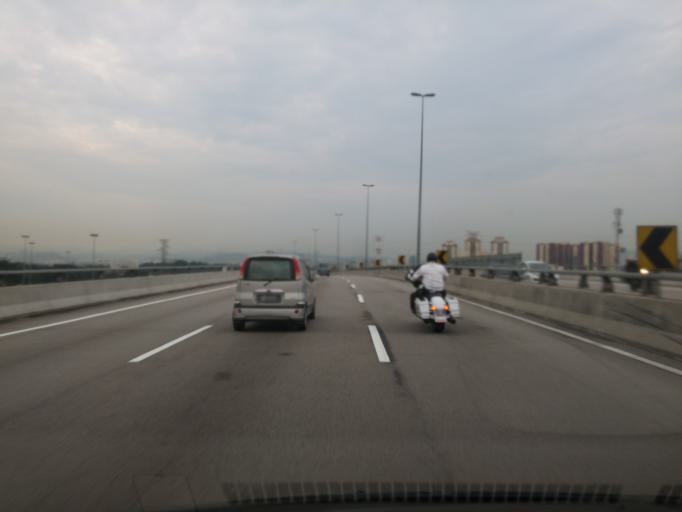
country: MY
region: Kuala Lumpur
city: Kuala Lumpur
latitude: 3.0996
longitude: 101.7014
